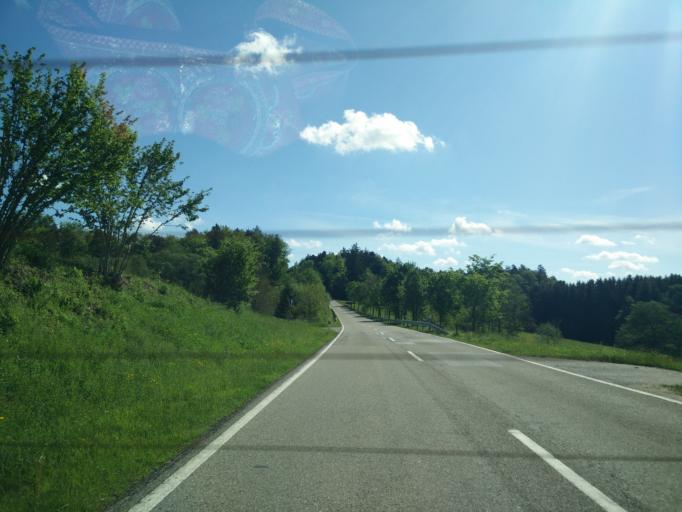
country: DE
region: Baden-Wuerttemberg
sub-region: Regierungsbezirk Stuttgart
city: Gschwend
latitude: 48.9348
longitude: 9.7578
